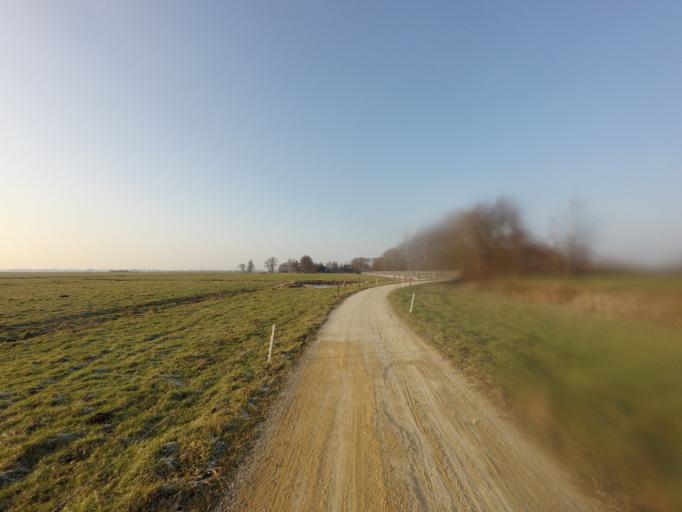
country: NL
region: South Holland
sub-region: Gemeente Vlist
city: Vlist
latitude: 51.9972
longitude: 4.8210
